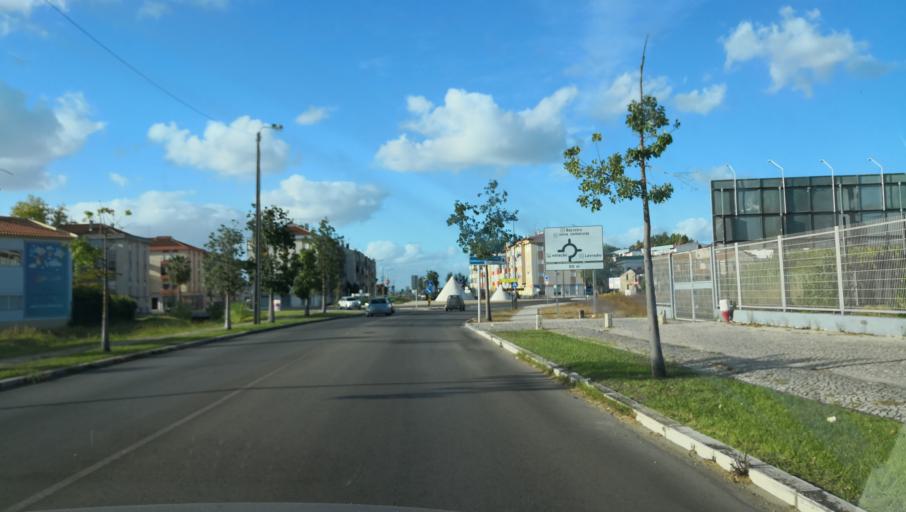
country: PT
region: Setubal
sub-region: Barreiro
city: Barreiro
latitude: 38.6640
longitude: -9.0554
